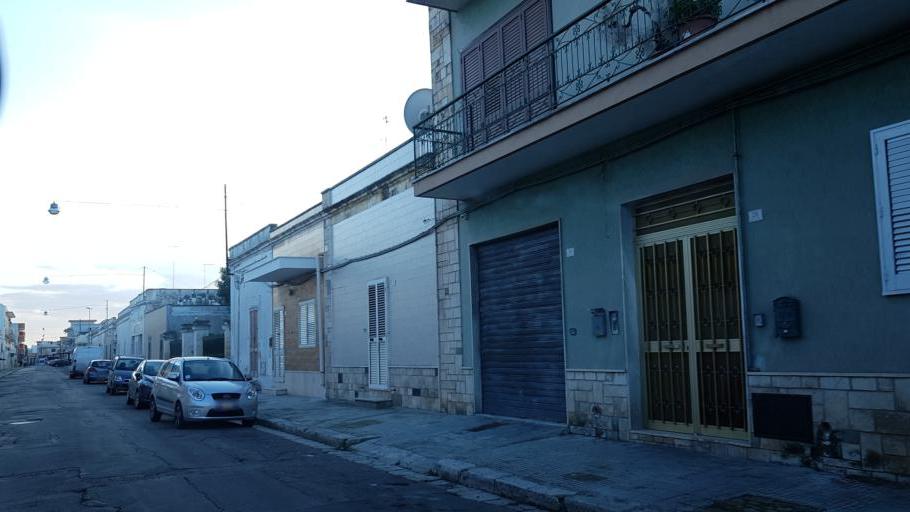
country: IT
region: Apulia
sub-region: Provincia di Lecce
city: Surbo
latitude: 40.3961
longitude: 18.1298
